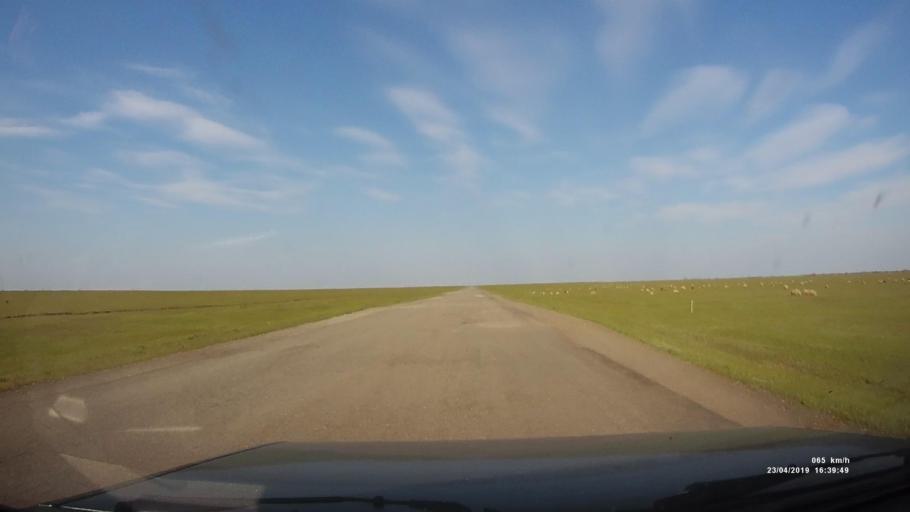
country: RU
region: Kalmykiya
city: Priyutnoye
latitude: 46.3410
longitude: 43.1705
